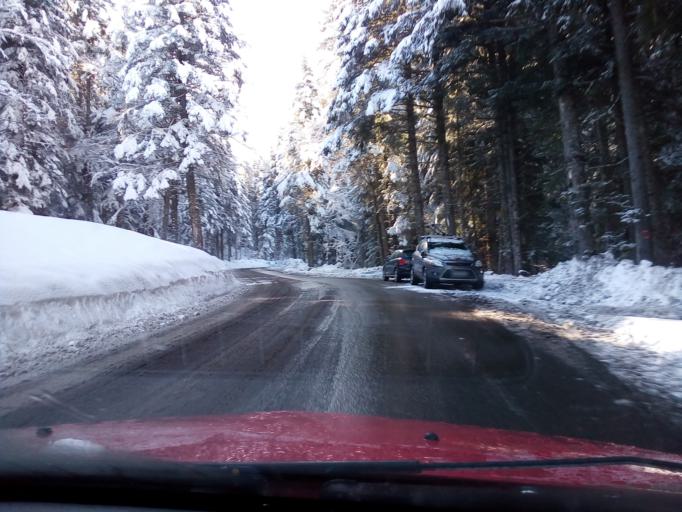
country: FR
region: Rhone-Alpes
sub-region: Departement de l'Isere
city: Le Sappey-en-Chartreuse
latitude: 45.3078
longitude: 5.7725
